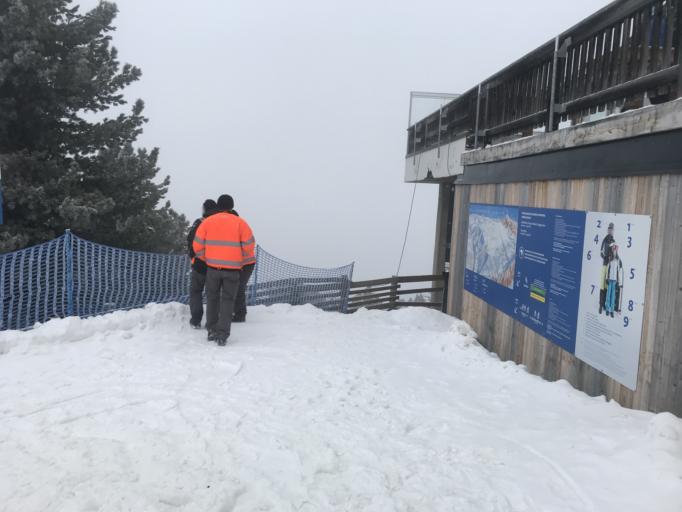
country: IT
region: Trentino-Alto Adige
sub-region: Bolzano
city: San Pietro
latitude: 46.6853
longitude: 11.7097
